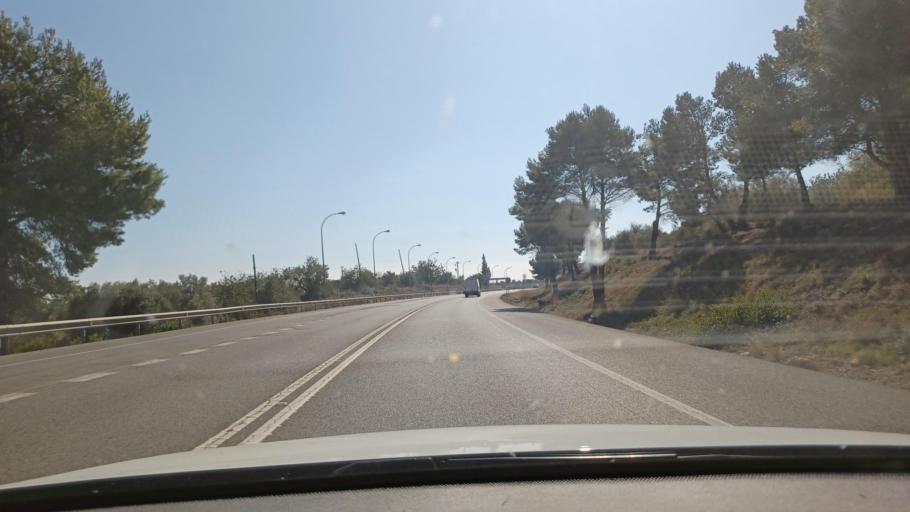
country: ES
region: Catalonia
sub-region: Provincia de Tarragona
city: L'Ampolla
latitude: 40.8407
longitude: 0.7112
